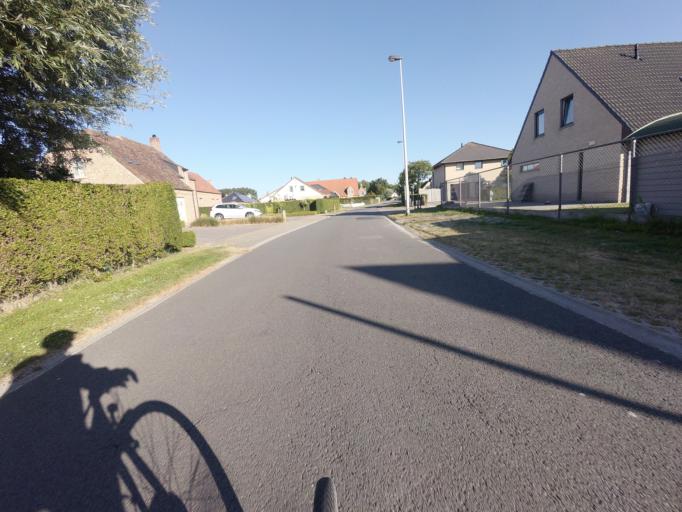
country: BE
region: Flanders
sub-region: Provincie West-Vlaanderen
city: Bredene
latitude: 51.2548
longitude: 2.9928
